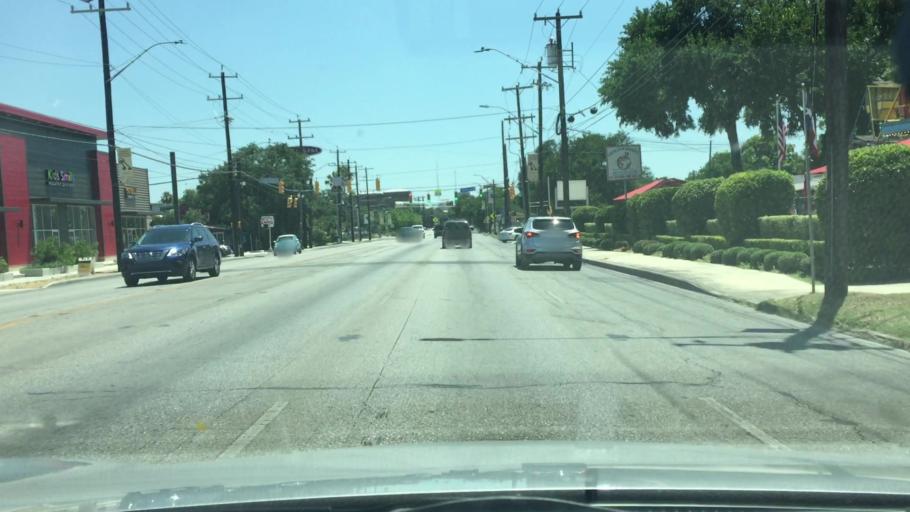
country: US
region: Texas
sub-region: Bexar County
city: Terrell Hills
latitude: 29.4551
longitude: -98.4711
